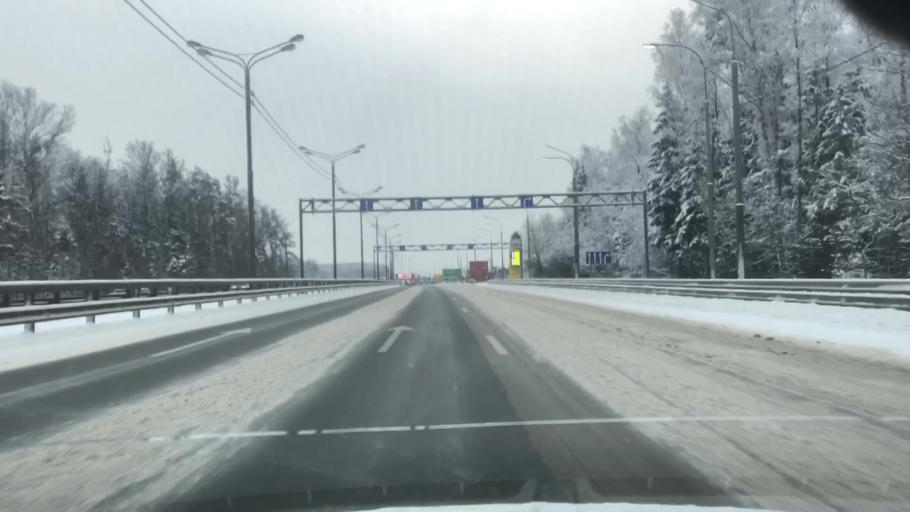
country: RU
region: Moskovskaya
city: Mikhnevo
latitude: 55.1749
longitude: 37.9112
